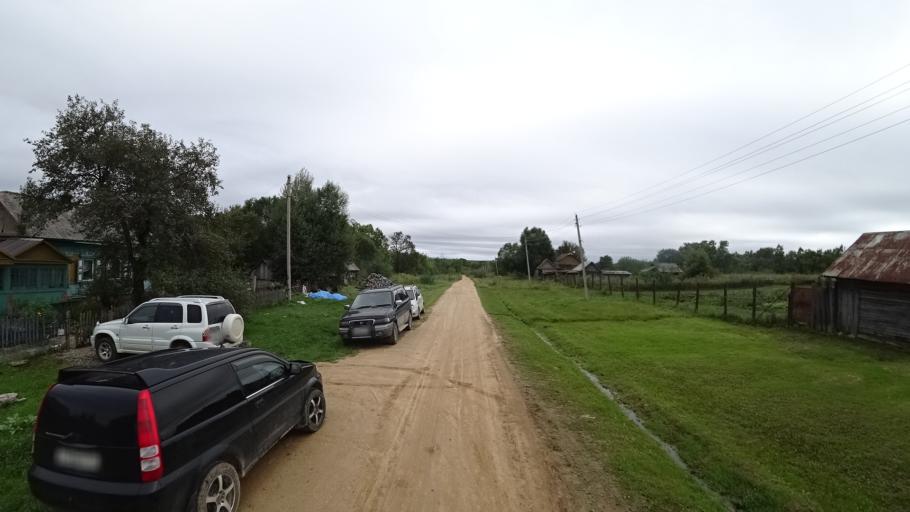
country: RU
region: Primorskiy
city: Rettikhovka
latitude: 44.1395
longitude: 132.6371
